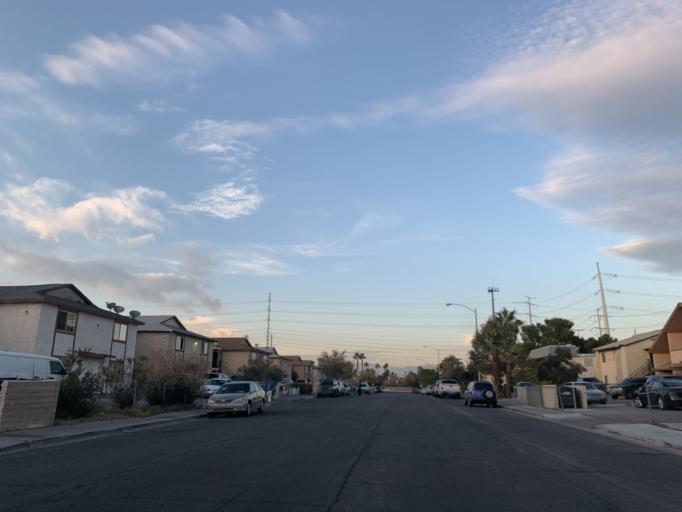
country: US
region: Nevada
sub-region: Clark County
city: Spring Valley
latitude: 36.1128
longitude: -115.2146
